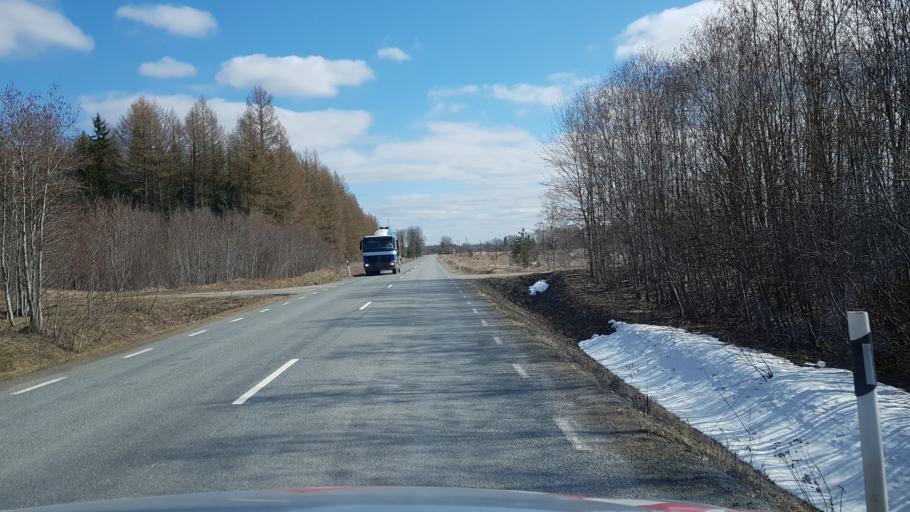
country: EE
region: Laeaene-Virumaa
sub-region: Tapa vald
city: Tapa
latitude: 59.2712
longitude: 25.9229
